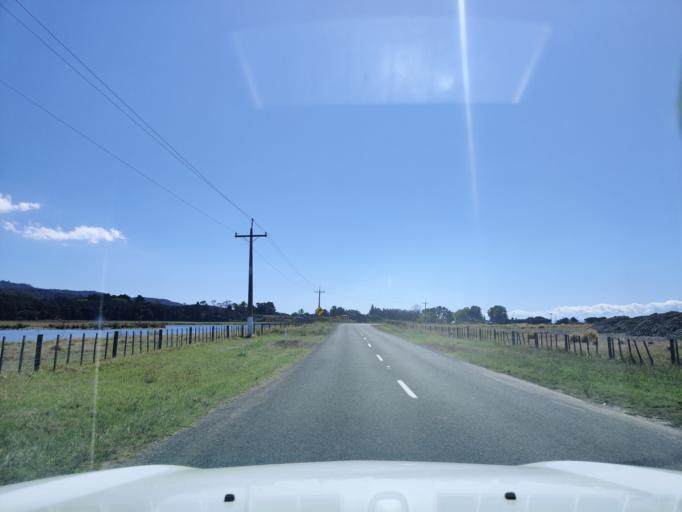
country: NZ
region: Waikato
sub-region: Thames-Coromandel District
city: Thames
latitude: -37.0614
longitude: 175.2983
